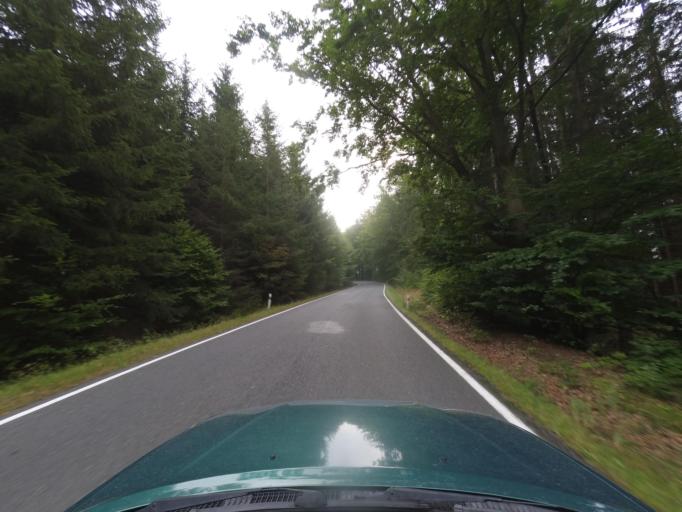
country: CZ
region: Plzensky
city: Bela nad Radbuzou
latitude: 49.5897
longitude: 12.6676
